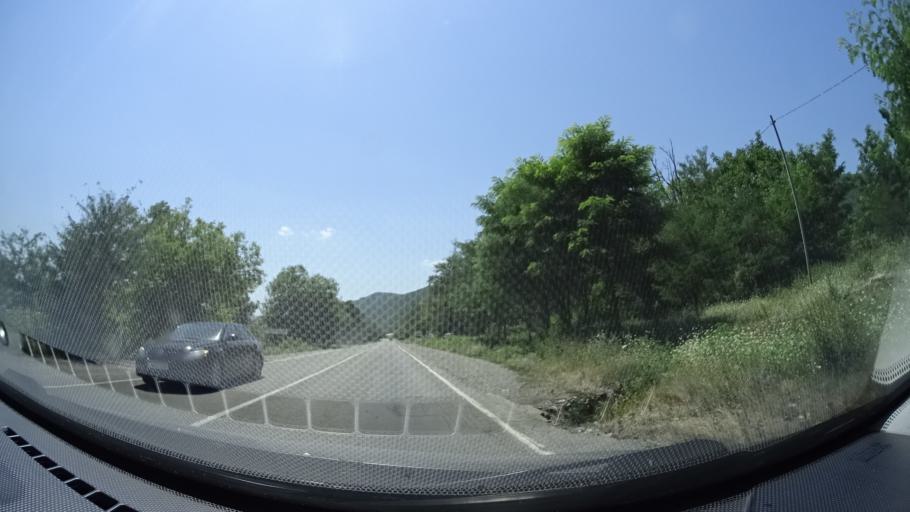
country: GE
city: Zhinvali
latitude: 42.1019
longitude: 44.7678
